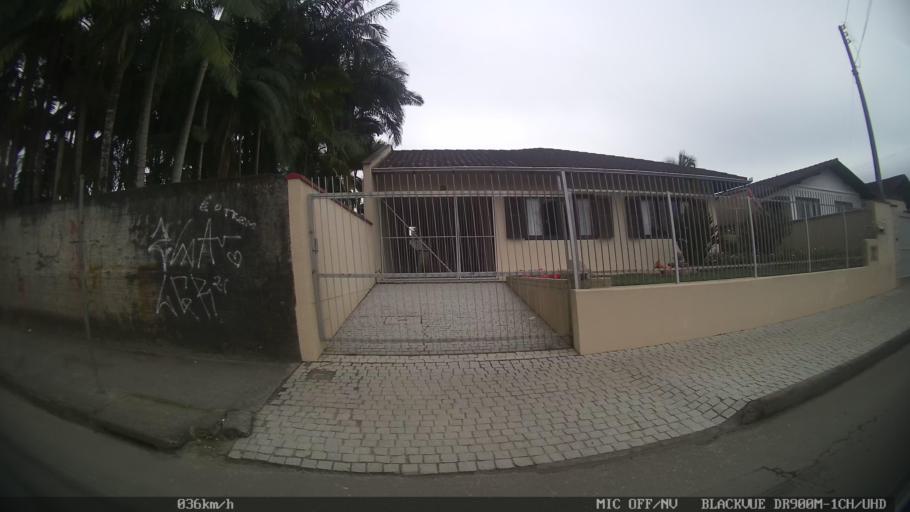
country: BR
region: Santa Catarina
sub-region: Joinville
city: Joinville
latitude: -26.2885
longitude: -48.9022
